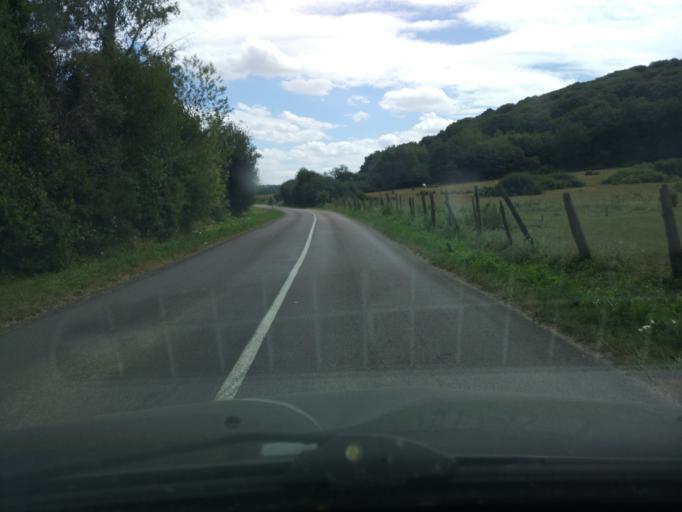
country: FR
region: Ile-de-France
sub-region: Departement de l'Essonne
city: Villiers-le-Bacle
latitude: 48.7148
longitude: 2.1182
